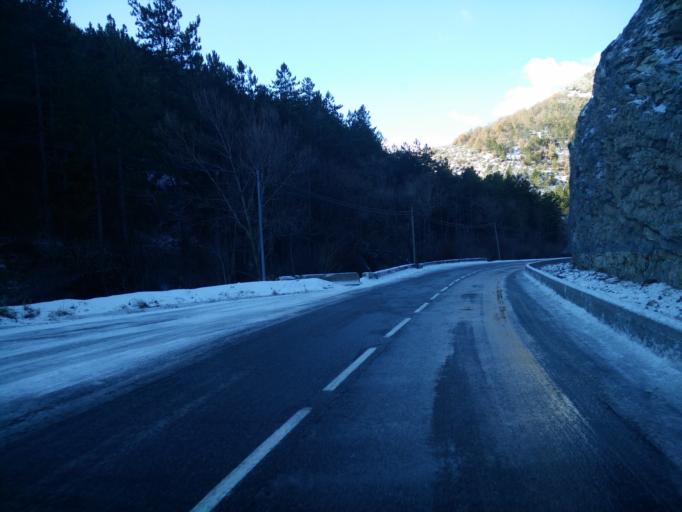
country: FR
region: Provence-Alpes-Cote d'Azur
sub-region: Departement des Alpes-de-Haute-Provence
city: Castellane
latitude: 43.9145
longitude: 6.5616
